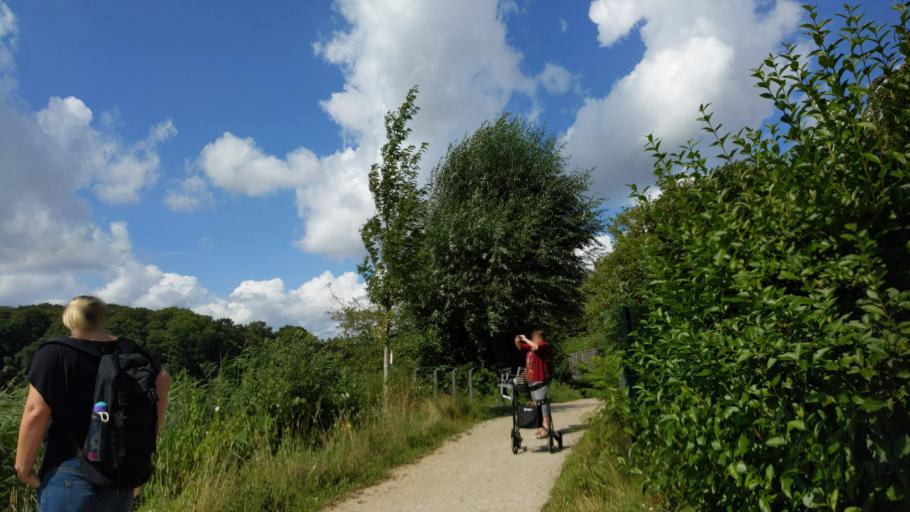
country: DE
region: Schleswig-Holstein
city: Reinfeld
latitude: 53.8336
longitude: 10.4861
